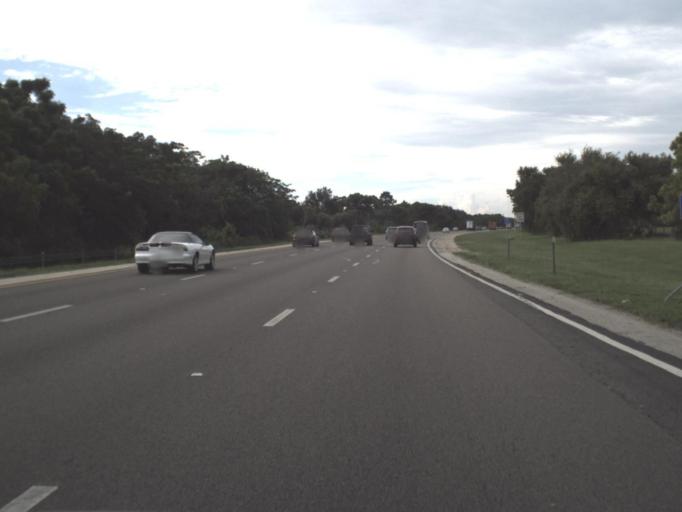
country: US
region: Florida
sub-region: Sarasota County
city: The Meadows
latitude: 27.3817
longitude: -82.4472
